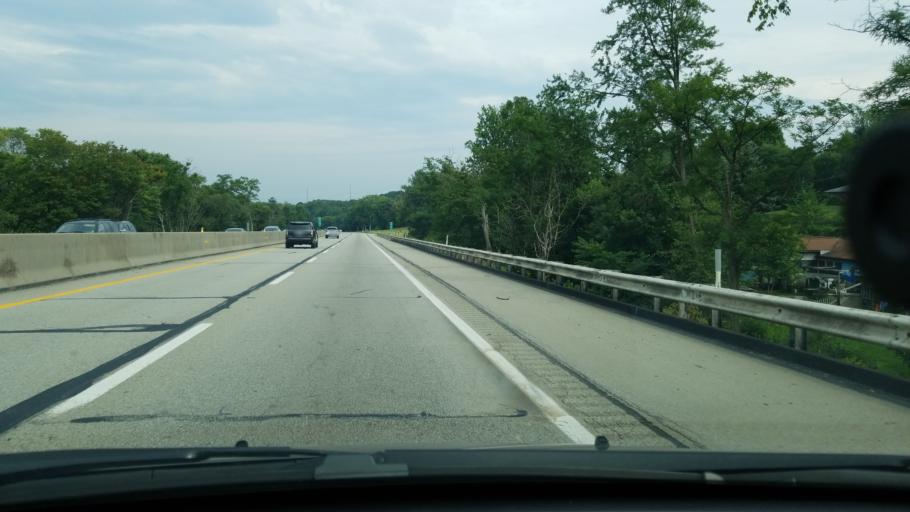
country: US
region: Pennsylvania
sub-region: Beaver County
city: Beaver Falls
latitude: 40.7926
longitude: -80.2740
